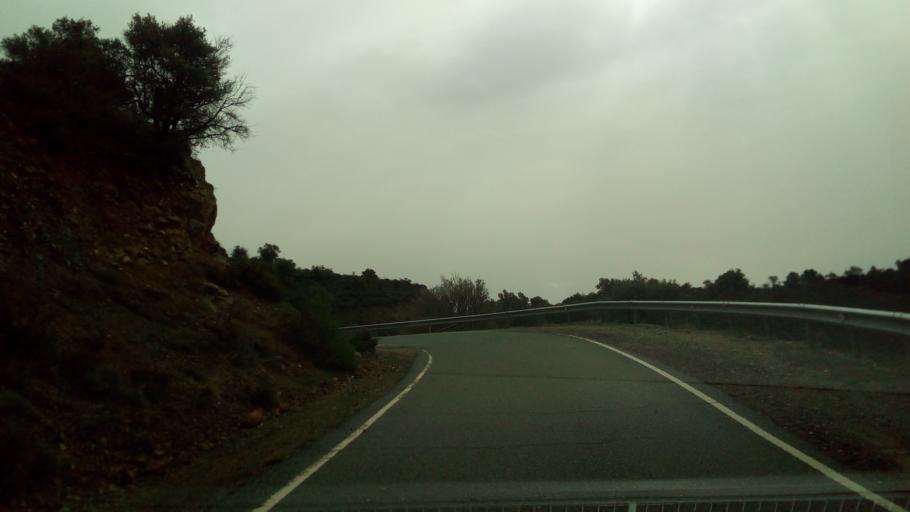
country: CY
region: Limassol
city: Mouttagiaka
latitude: 34.8075
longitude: 33.0887
